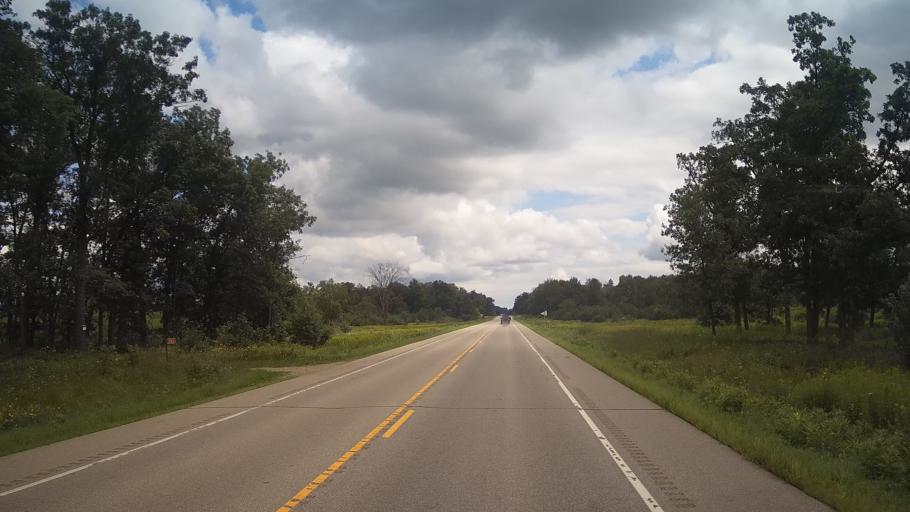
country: US
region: Wisconsin
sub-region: Adams County
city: Friendship
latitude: 44.0255
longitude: -89.6832
